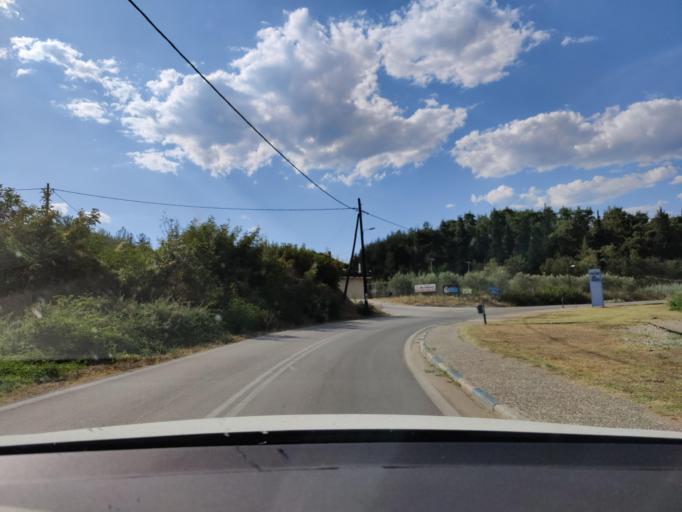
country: GR
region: Central Macedonia
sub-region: Nomos Serron
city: Chrysochorafa
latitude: 41.1384
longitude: 23.2186
